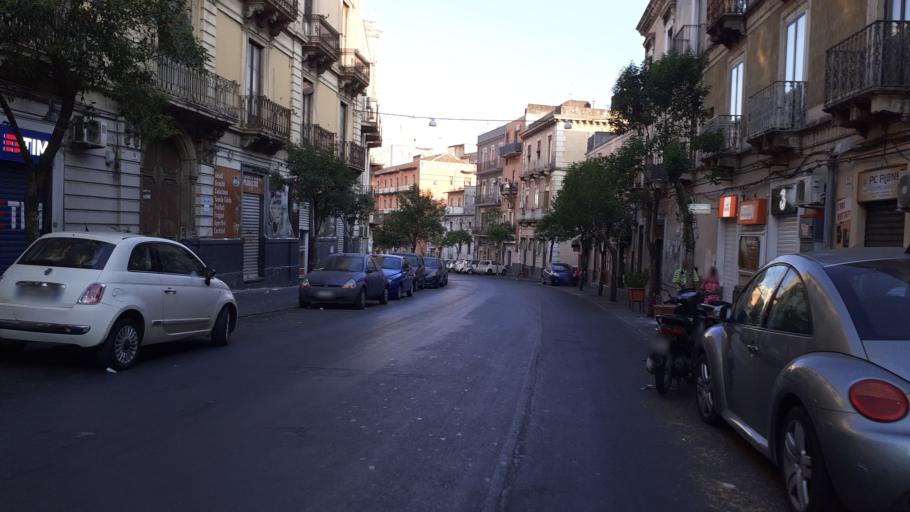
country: IT
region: Sicily
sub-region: Catania
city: Catania
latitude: 37.5000
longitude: 15.0763
